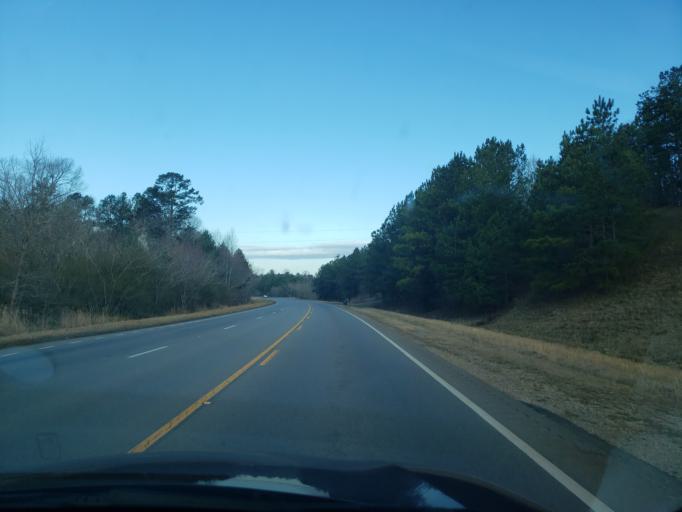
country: US
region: Alabama
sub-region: Cleburne County
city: Heflin
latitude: 33.5004
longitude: -85.6029
